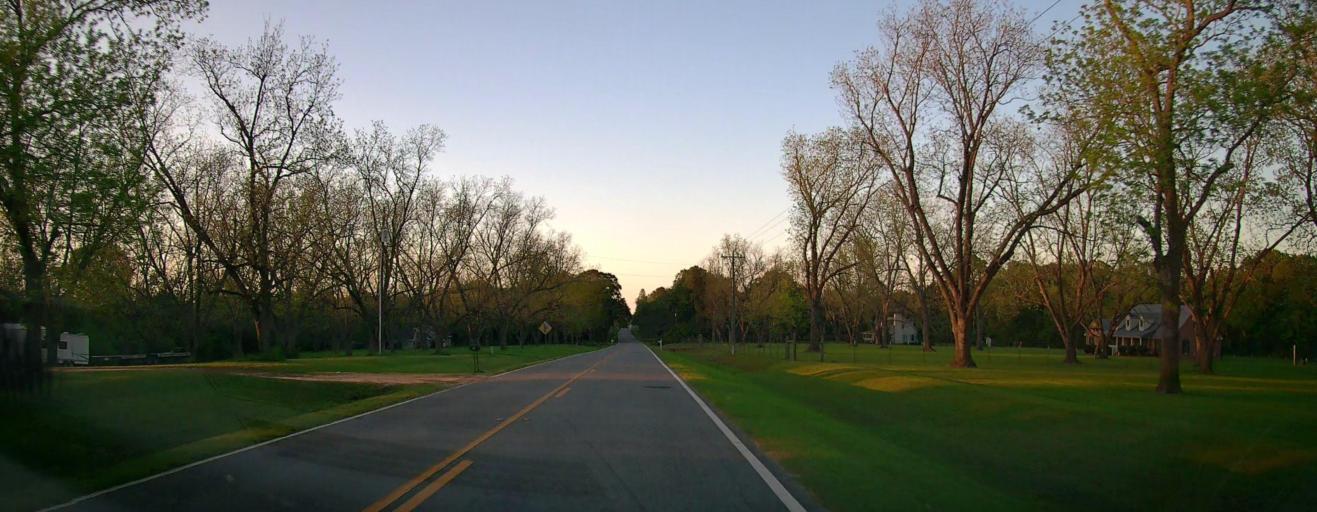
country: US
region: Georgia
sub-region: Ben Hill County
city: Fitzgerald
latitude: 31.7197
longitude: -83.3100
